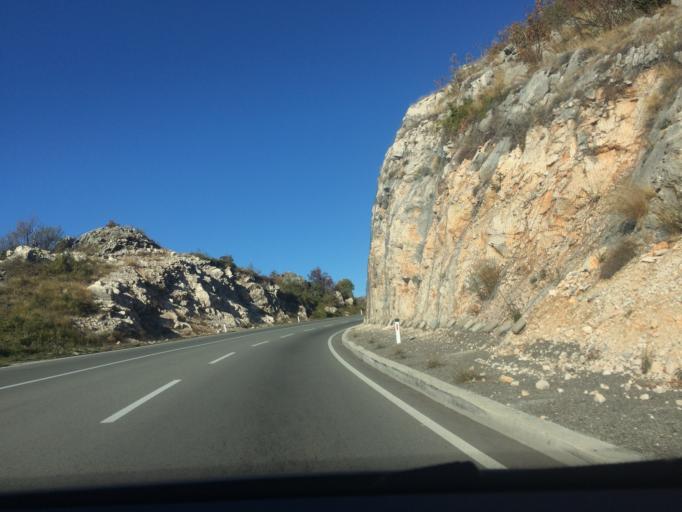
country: ME
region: Cetinje
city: Cetinje
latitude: 42.3822
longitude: 18.9496
